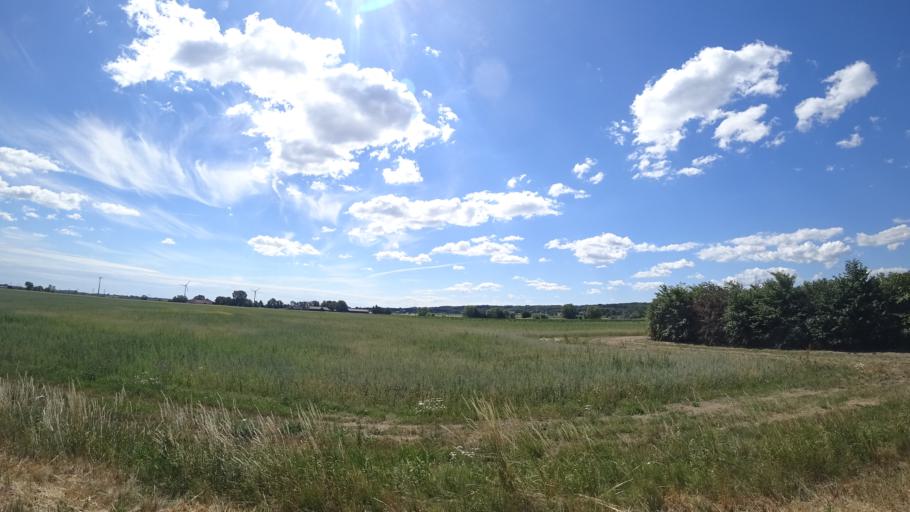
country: SE
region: Skane
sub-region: Kristianstads Kommun
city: Onnestad
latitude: 56.0574
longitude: 14.0309
